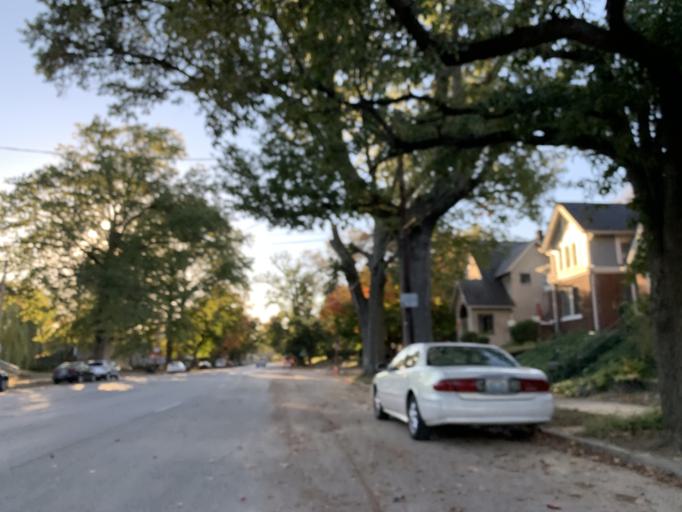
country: US
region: Indiana
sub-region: Floyd County
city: New Albany
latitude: 38.2747
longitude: -85.8057
